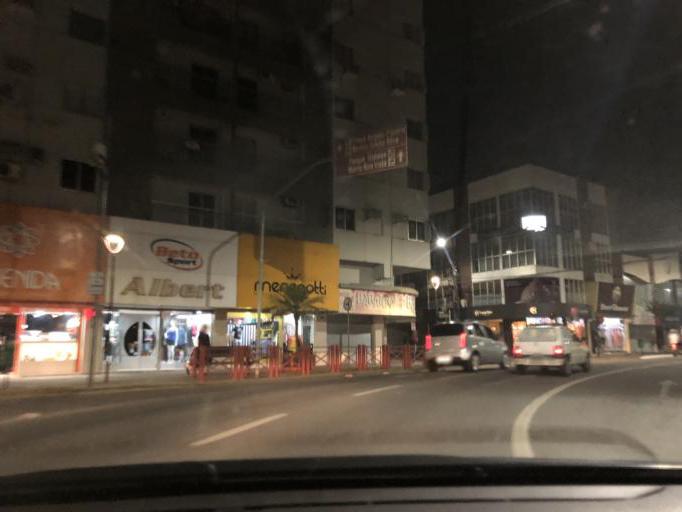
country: BR
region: Santa Catarina
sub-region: Jaragua Do Sul
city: Jaragua do Sul
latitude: -26.4852
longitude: -49.0829
